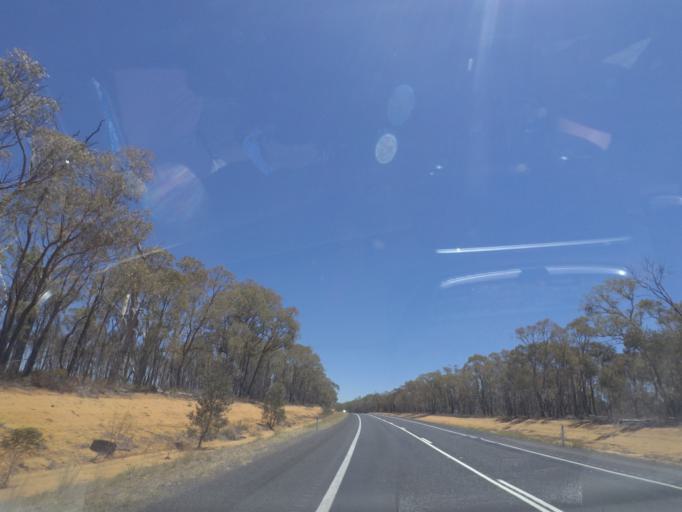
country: AU
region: New South Wales
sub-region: Warrumbungle Shire
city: Coonabarabran
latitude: -31.2038
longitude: 149.3371
